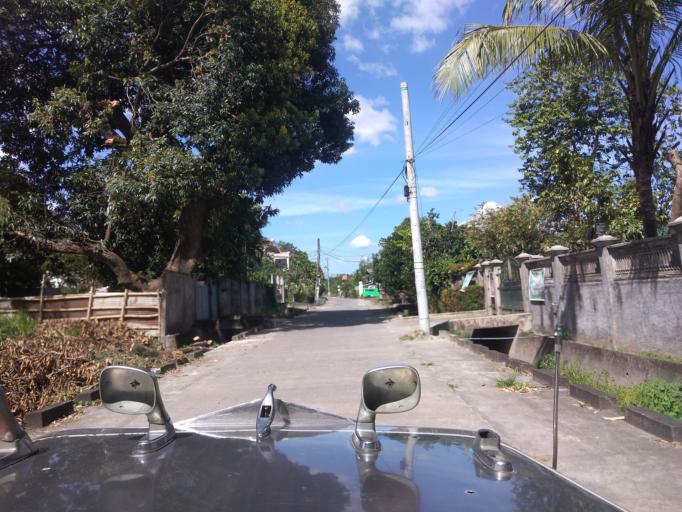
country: PH
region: Central Luzon
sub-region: Province of Pampanga
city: Santa Rita
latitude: 15.0045
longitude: 120.5993
